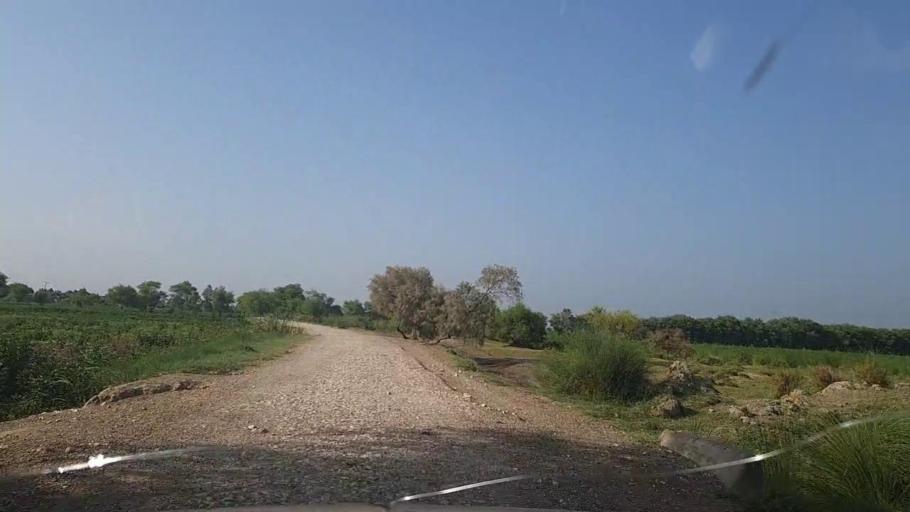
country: PK
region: Sindh
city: Khanpur
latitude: 27.7089
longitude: 69.3319
